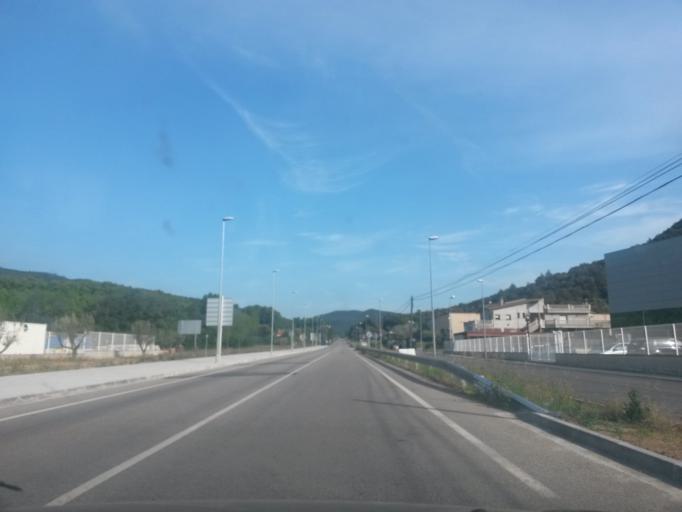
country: ES
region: Catalonia
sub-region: Provincia de Girona
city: la Cellera de Ter
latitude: 42.0198
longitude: 2.5943
